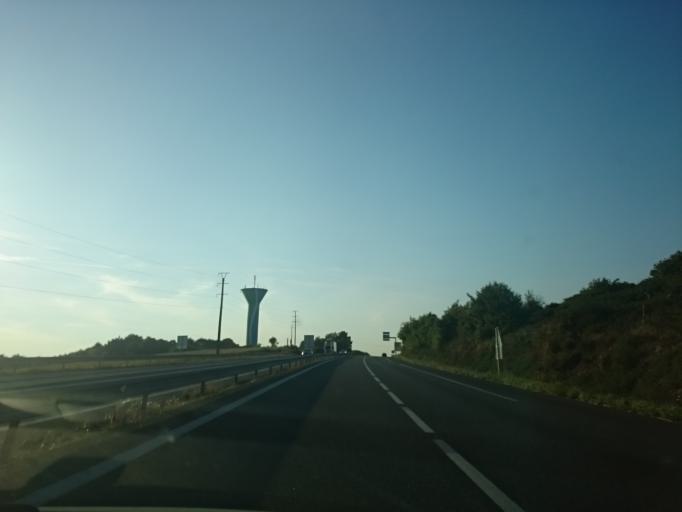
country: FR
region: Brittany
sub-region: Departement du Morbihan
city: Muzillac
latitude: 47.5545
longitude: -2.4941
